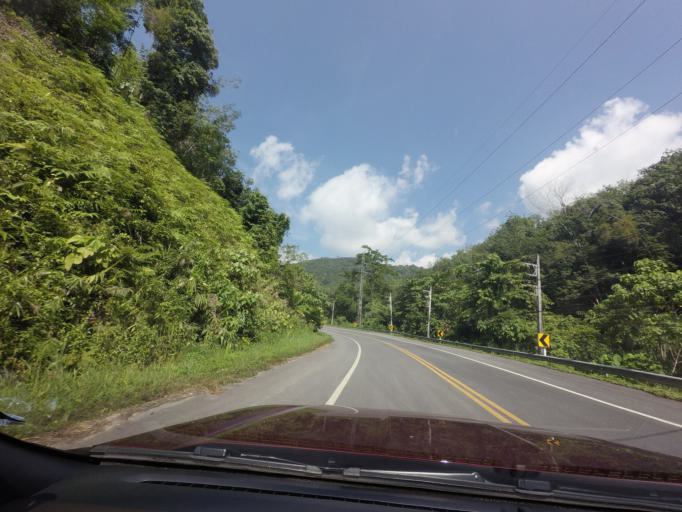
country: TH
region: Yala
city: Betong
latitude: 5.9197
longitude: 101.1614
